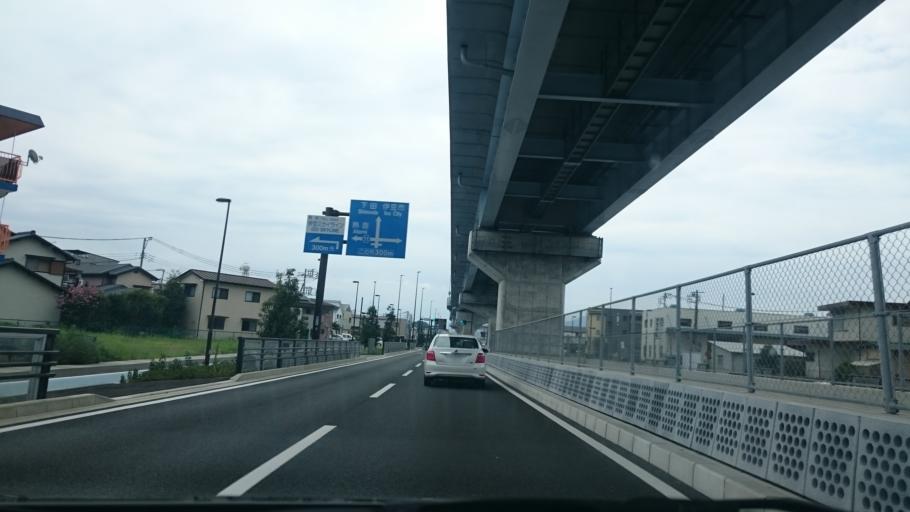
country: JP
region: Shizuoka
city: Mishima
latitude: 35.0901
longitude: 138.9462
